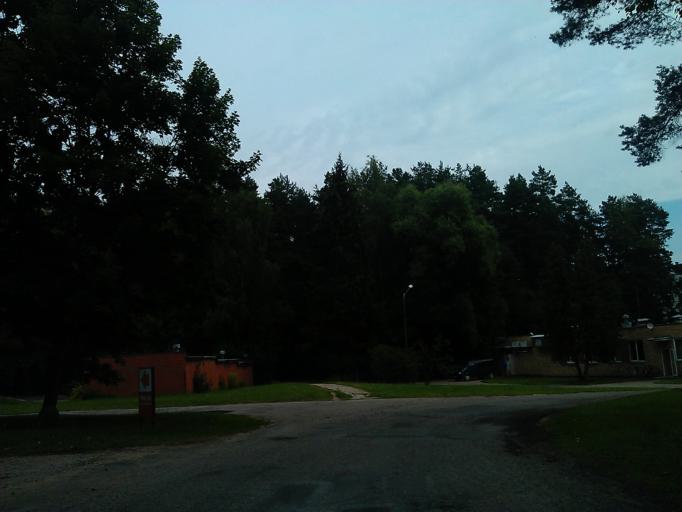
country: LV
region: Valmieras Rajons
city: Valmiera
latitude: 57.5198
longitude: 25.3879
